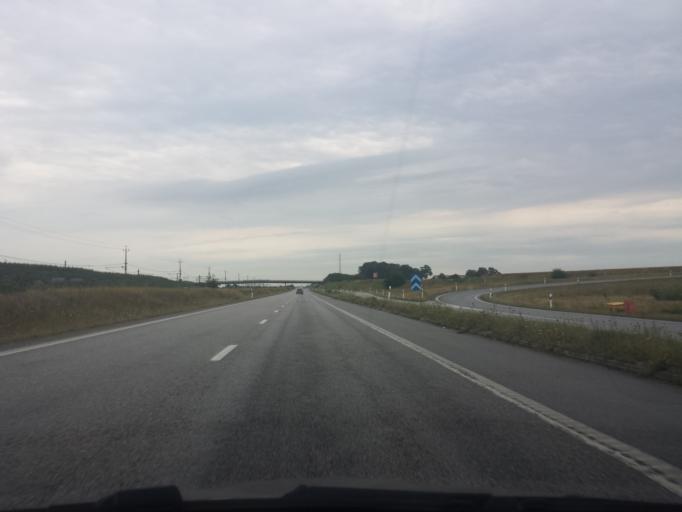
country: SE
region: Skane
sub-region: Malmo
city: Tygelsjo
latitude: 55.5472
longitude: 13.0030
